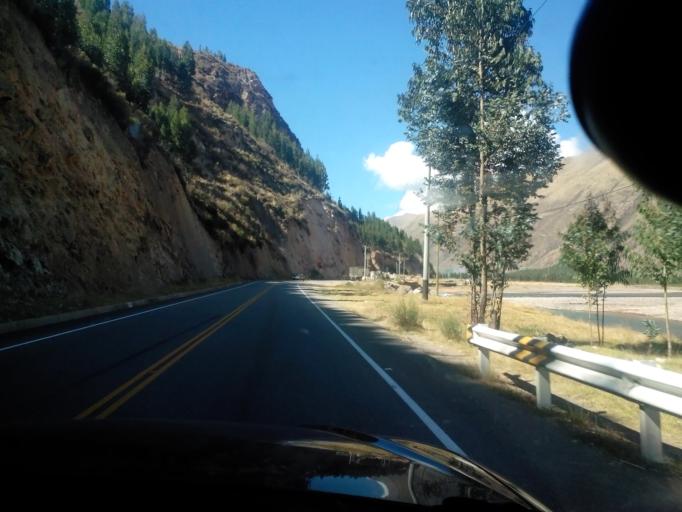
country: PE
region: Cusco
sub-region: Provincia de Quispicanchis
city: Urcos
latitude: -13.7295
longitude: -71.6017
